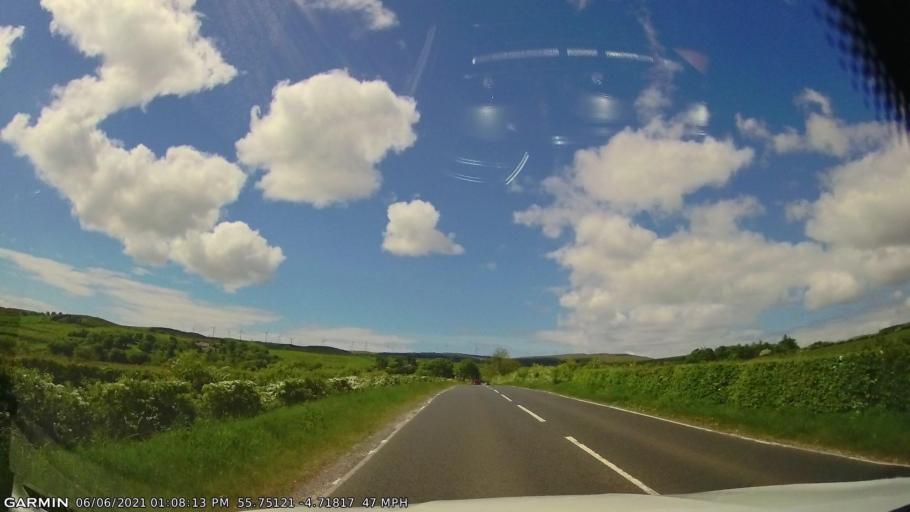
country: GB
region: Scotland
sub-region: North Ayrshire
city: Kilbirnie
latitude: 55.7512
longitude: -4.7181
